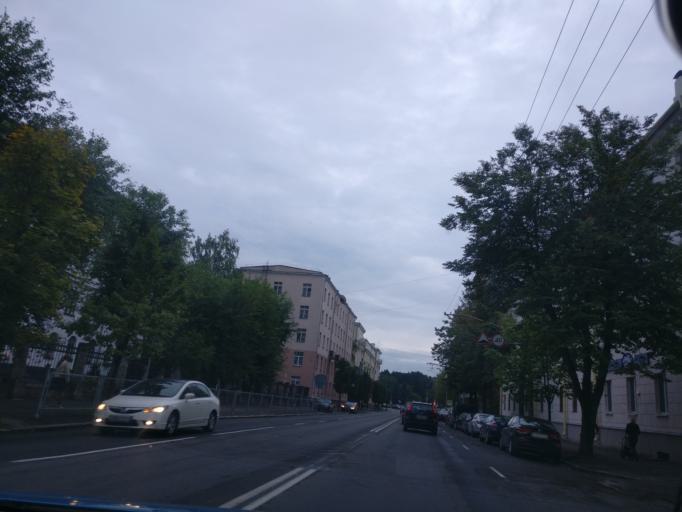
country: BY
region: Minsk
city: Minsk
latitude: 53.9251
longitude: 27.6076
